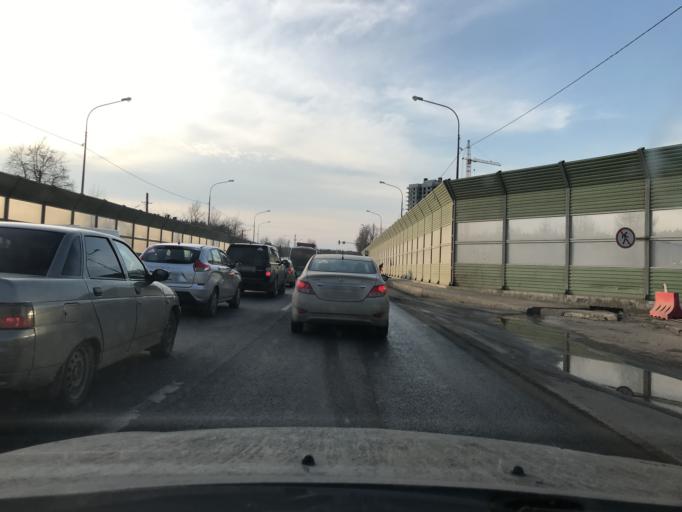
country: RU
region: Kaluga
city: Mstikhino
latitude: 54.5356
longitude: 36.1628
